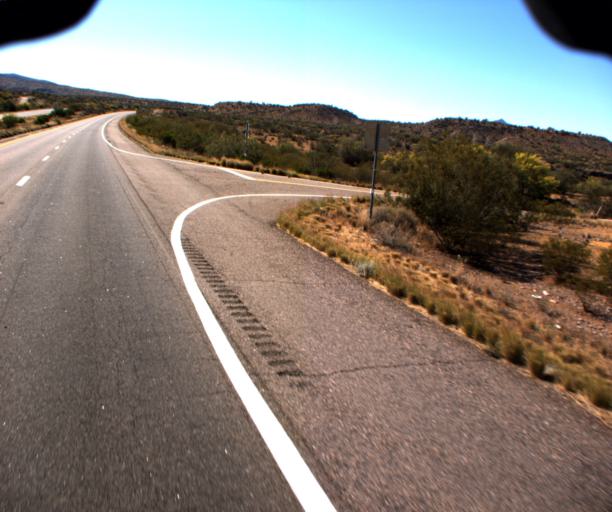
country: US
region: Arizona
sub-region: Yavapai County
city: Bagdad
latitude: 34.6274
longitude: -113.5390
